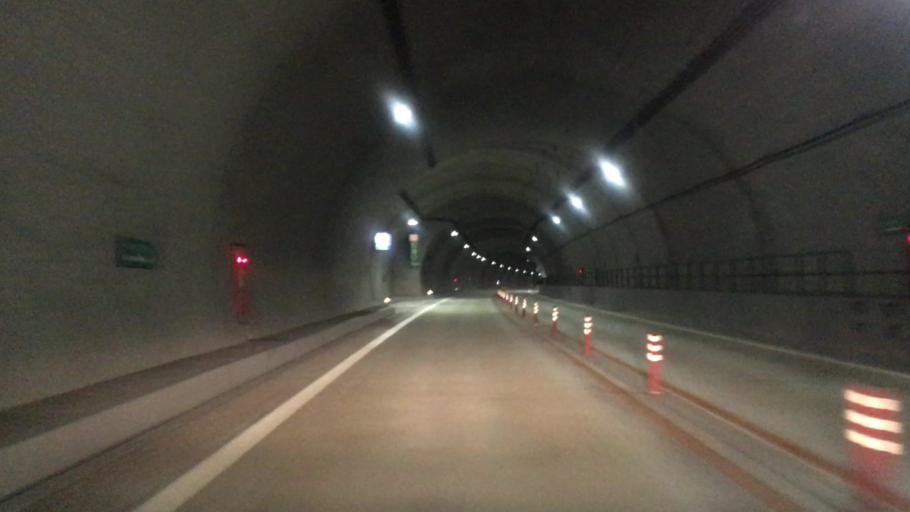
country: JP
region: Tottori
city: Tottori
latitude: 35.5629
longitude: 134.2859
